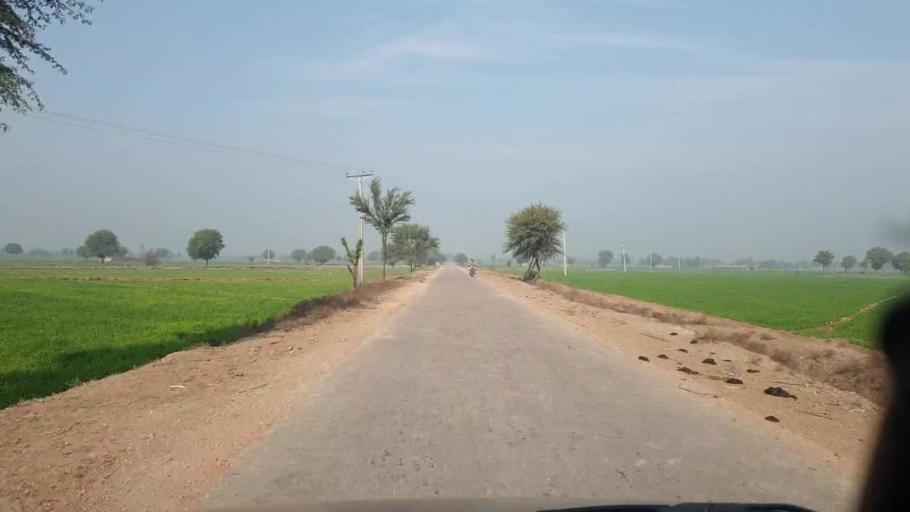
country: PK
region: Sindh
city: Shahdadpur
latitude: 26.0011
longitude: 68.5558
